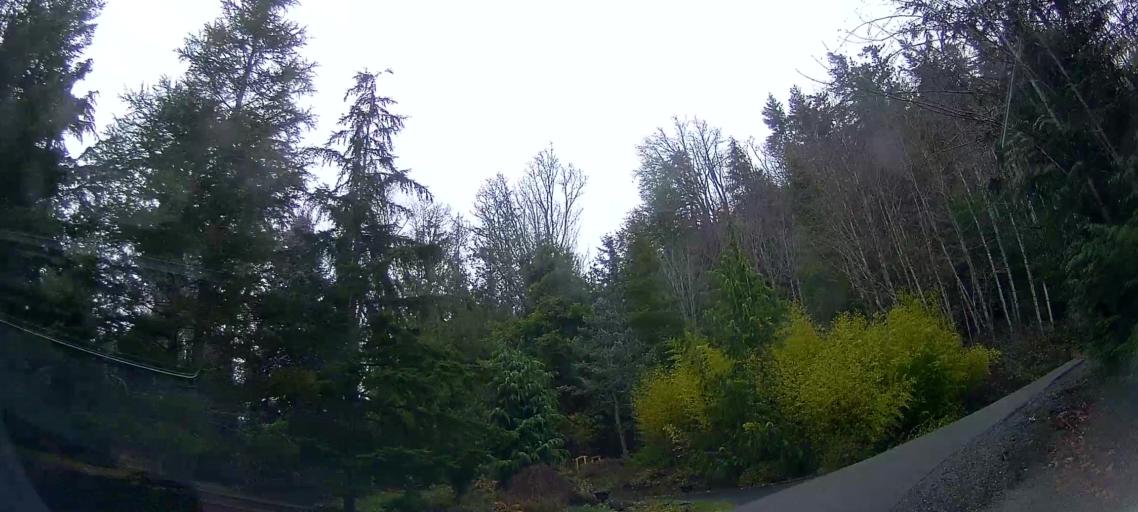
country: US
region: Washington
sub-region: Skagit County
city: Big Lake
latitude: 48.3839
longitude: -122.2901
